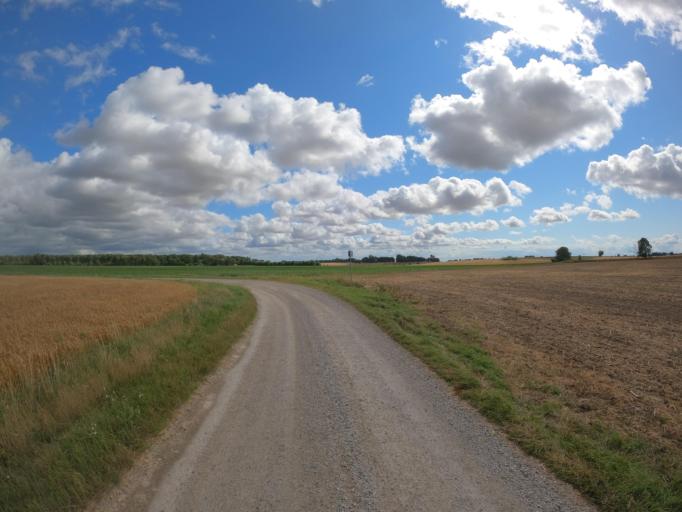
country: SE
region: Skane
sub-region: Lunds Kommun
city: Lund
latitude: 55.7276
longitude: 13.2627
